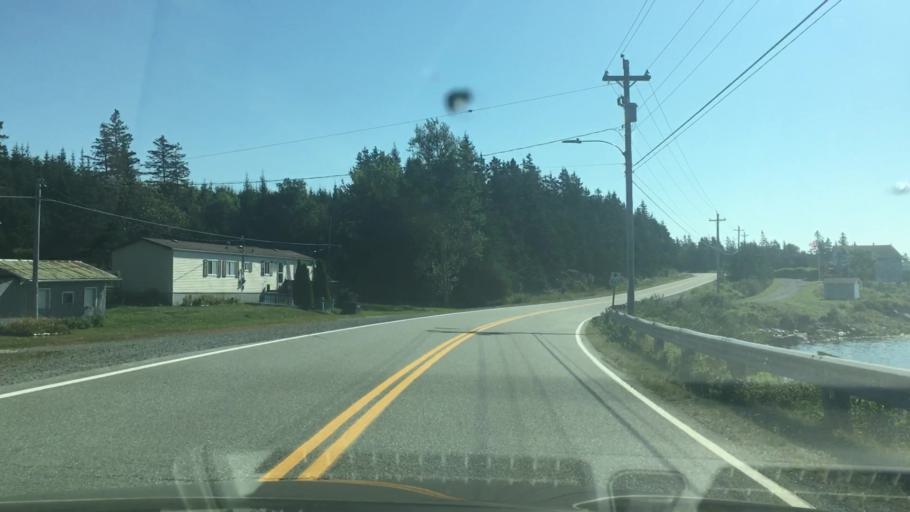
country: CA
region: Nova Scotia
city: Cole Harbour
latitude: 44.8049
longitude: -62.7064
